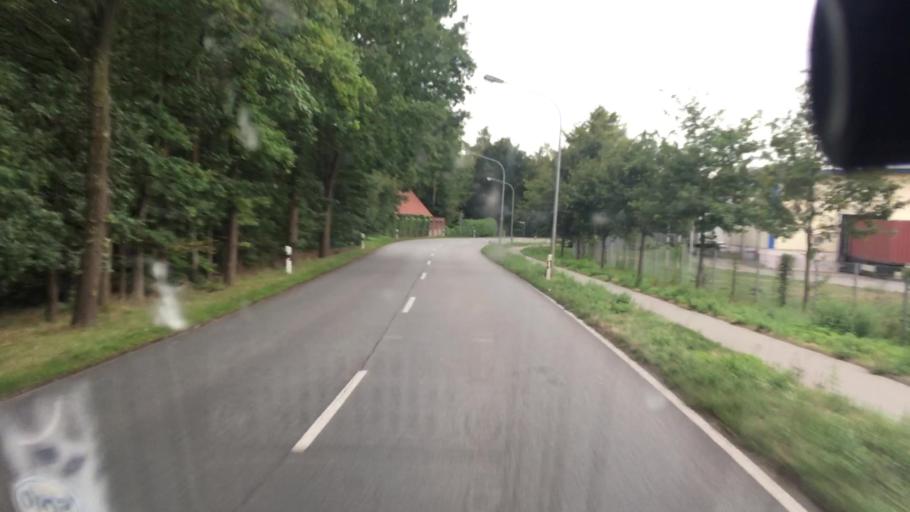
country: DE
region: Lower Saxony
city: Lohne
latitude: 52.6577
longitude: 8.1955
